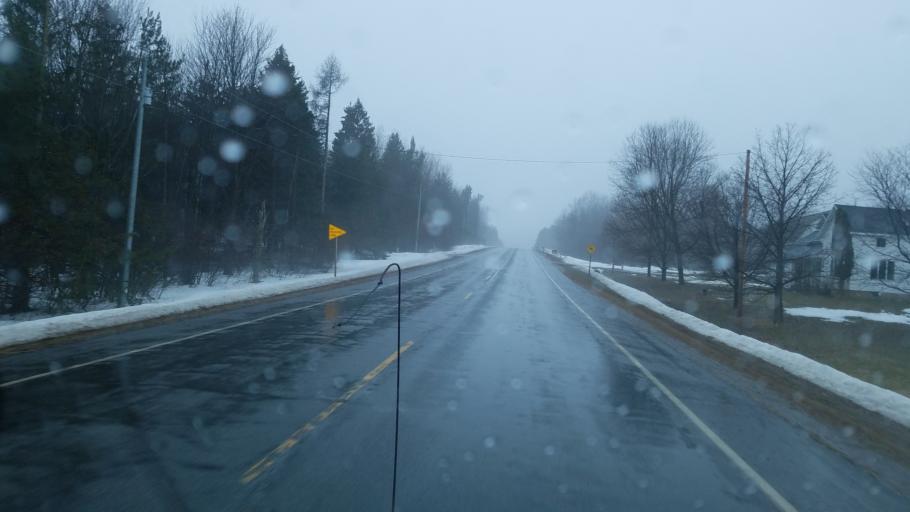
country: US
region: Wisconsin
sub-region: Wood County
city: Marshfield
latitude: 44.6779
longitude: -90.2493
